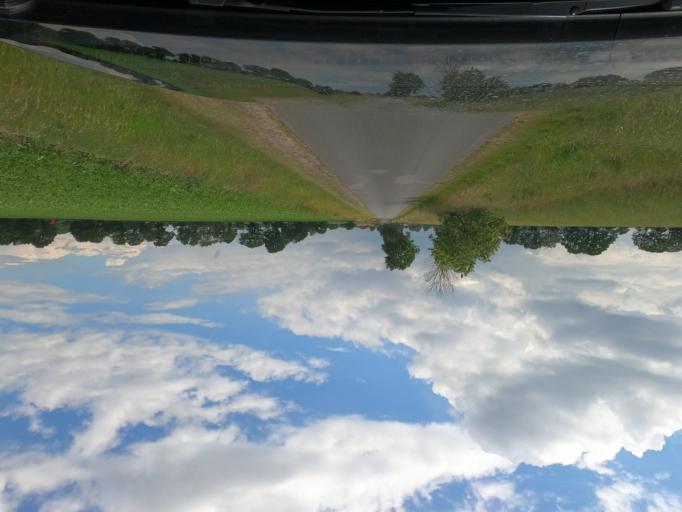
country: DE
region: Lower Saxony
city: Steimbke
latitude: 52.6293
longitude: 9.4116
